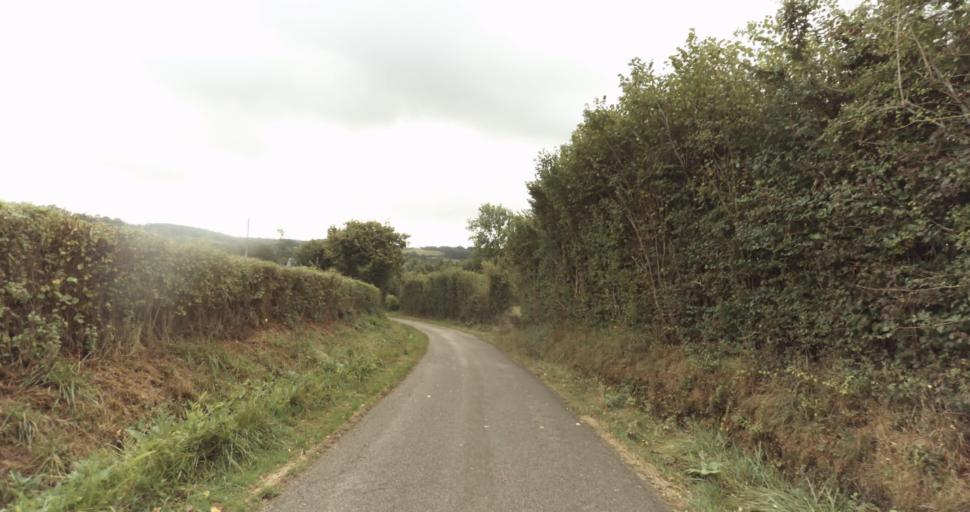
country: FR
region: Lower Normandy
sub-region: Departement de l'Orne
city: Gace
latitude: 48.8720
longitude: 0.2740
